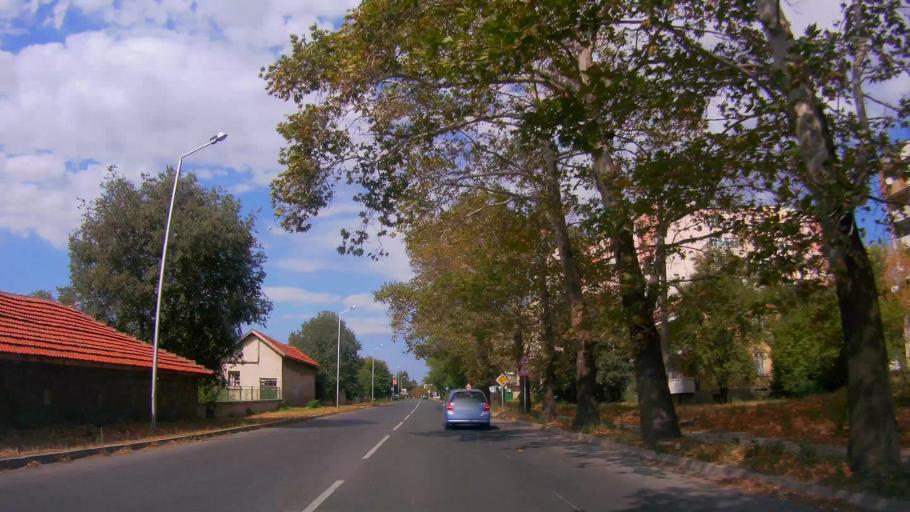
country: BG
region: Burgas
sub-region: Obshtina Aytos
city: Aytos
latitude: 42.6974
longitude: 27.2581
